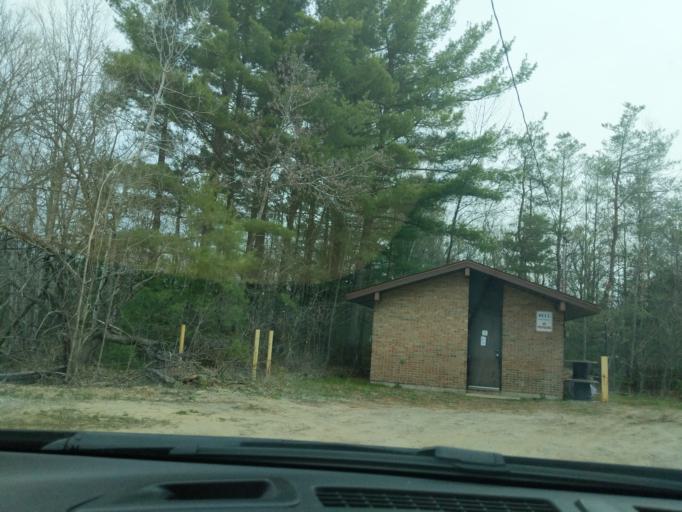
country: CA
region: Ontario
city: Orangeville
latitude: 43.9978
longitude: -80.0034
